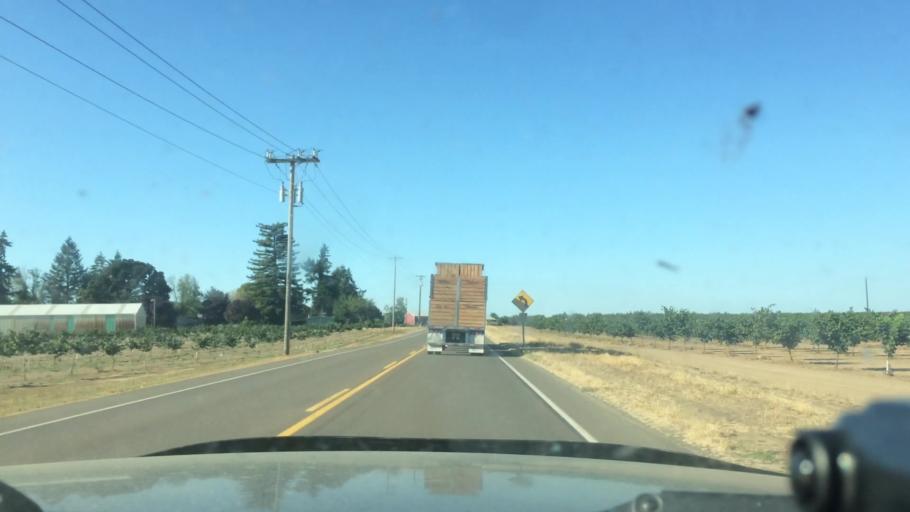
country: US
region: Oregon
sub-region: Marion County
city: Gervais
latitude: 45.0763
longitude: -122.9772
